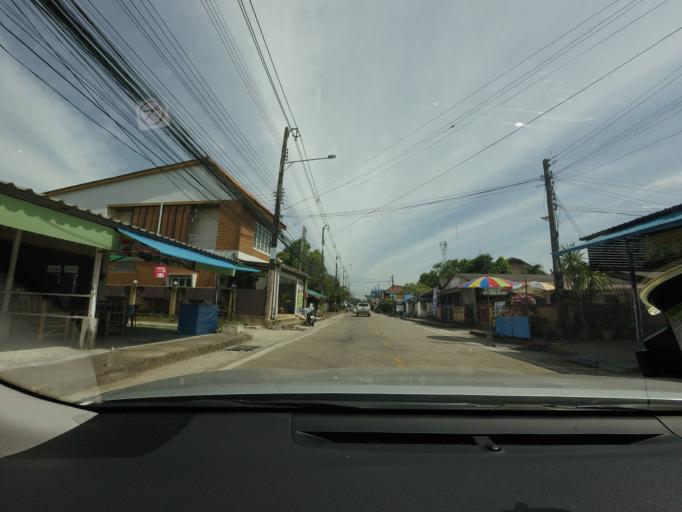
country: TH
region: Narathiwat
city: Narathiwat
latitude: 6.4225
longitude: 101.8169
